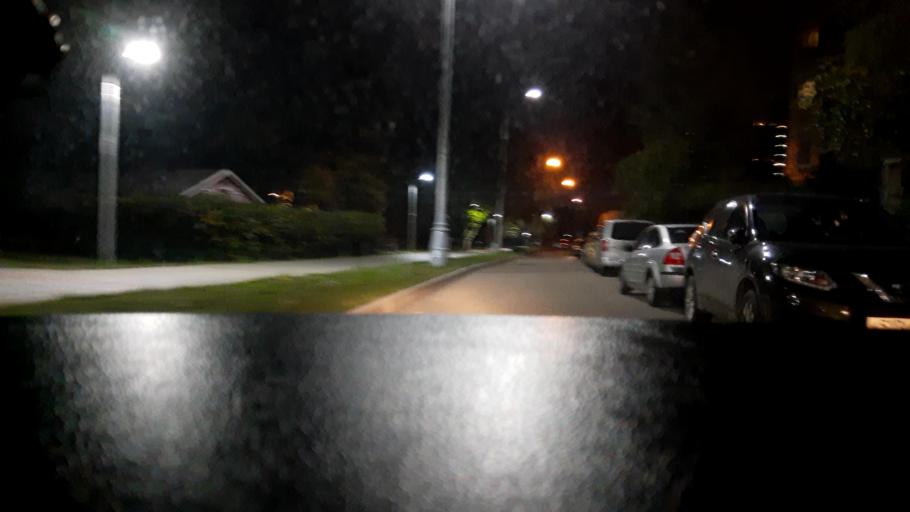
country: RU
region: Moscow
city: Tyoply Stan
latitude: 55.6295
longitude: 37.4790
